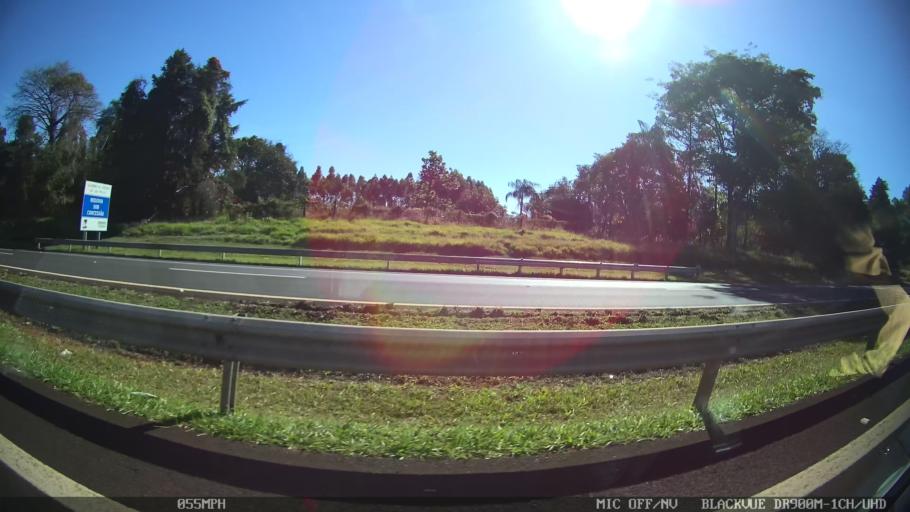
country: BR
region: Sao Paulo
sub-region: Franca
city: Franca
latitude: -20.5773
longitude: -47.3491
